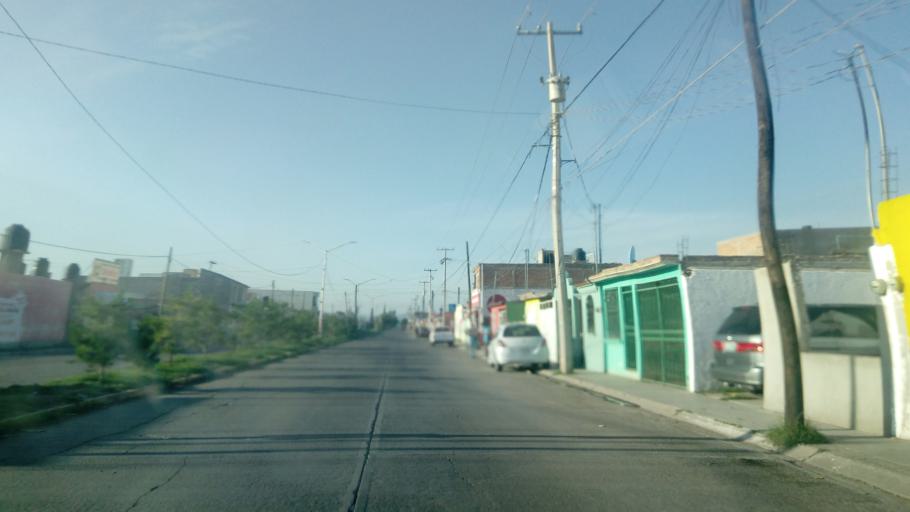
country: MX
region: Durango
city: Victoria de Durango
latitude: 24.0635
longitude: -104.5856
